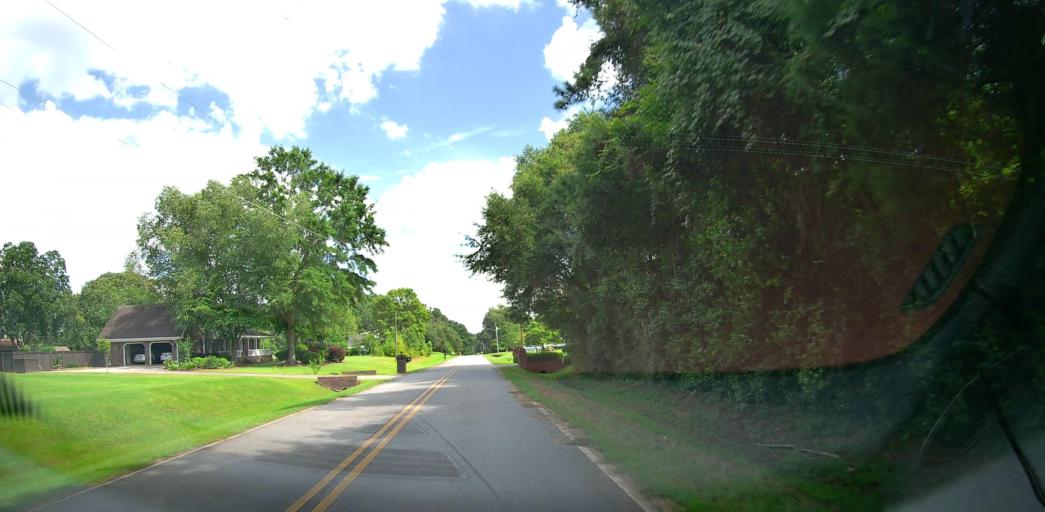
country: US
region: Georgia
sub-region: Houston County
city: Centerville
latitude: 32.5826
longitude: -83.6677
